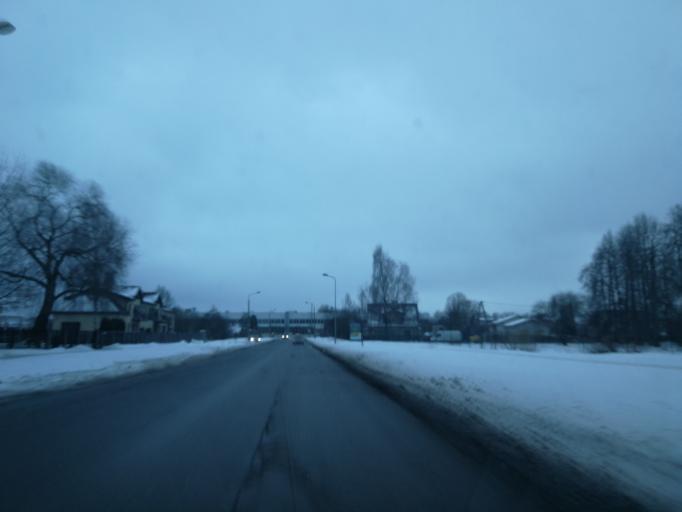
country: LV
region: Riga
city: Riga
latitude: 56.9427
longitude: 24.1746
